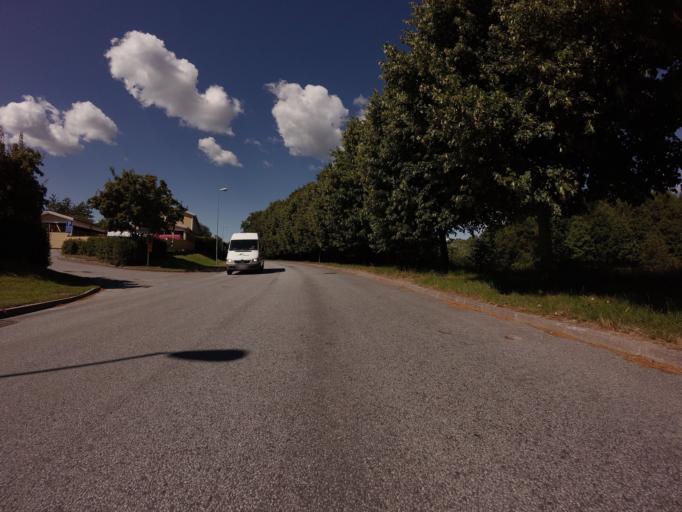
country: SE
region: Stockholm
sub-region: Upplands Vasby Kommun
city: Upplands Vaesby
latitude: 59.4621
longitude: 17.8973
